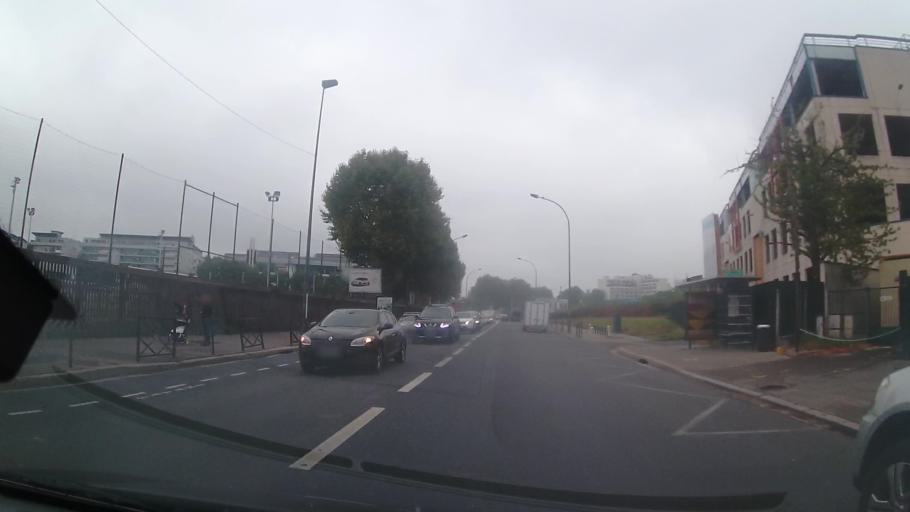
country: FR
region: Ile-de-France
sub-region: Departement des Hauts-de-Seine
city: Clichy
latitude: 48.9087
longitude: 2.3130
